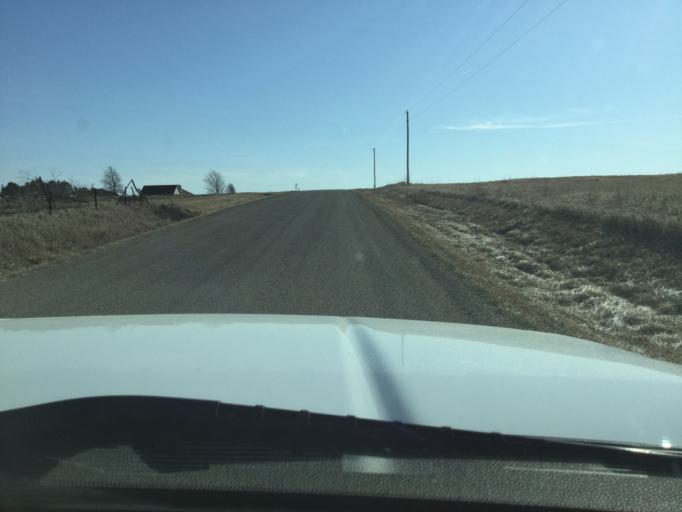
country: US
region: Kansas
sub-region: Brown County
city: Horton
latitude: 39.7256
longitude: -95.4542
